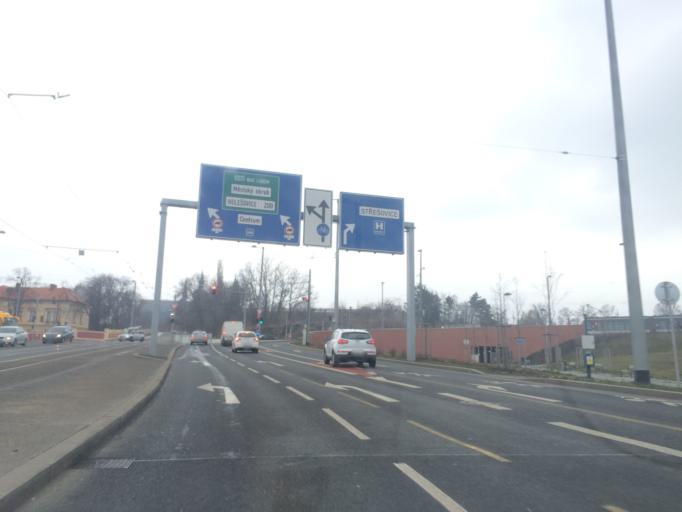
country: CZ
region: Praha
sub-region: Praha 1
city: Mala Strana
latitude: 50.0959
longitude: 14.3960
